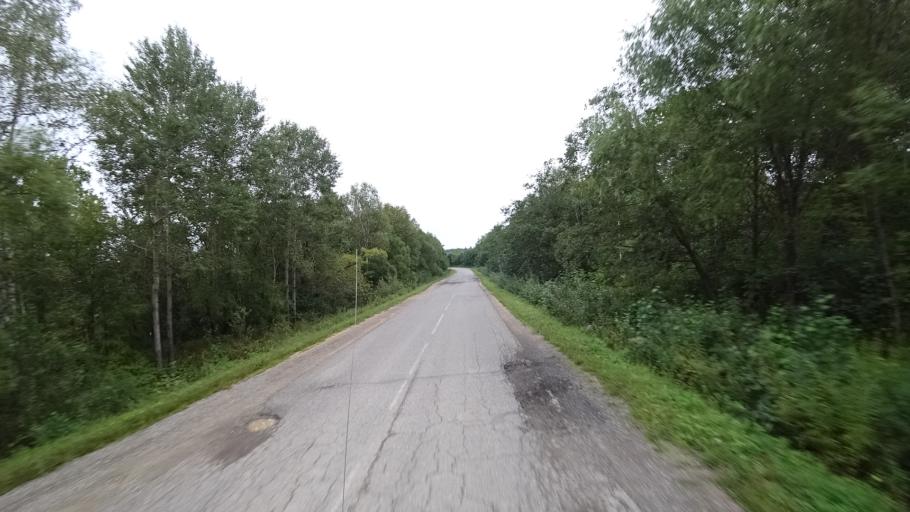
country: RU
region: Primorskiy
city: Rettikhovka
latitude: 44.1666
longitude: 132.7831
